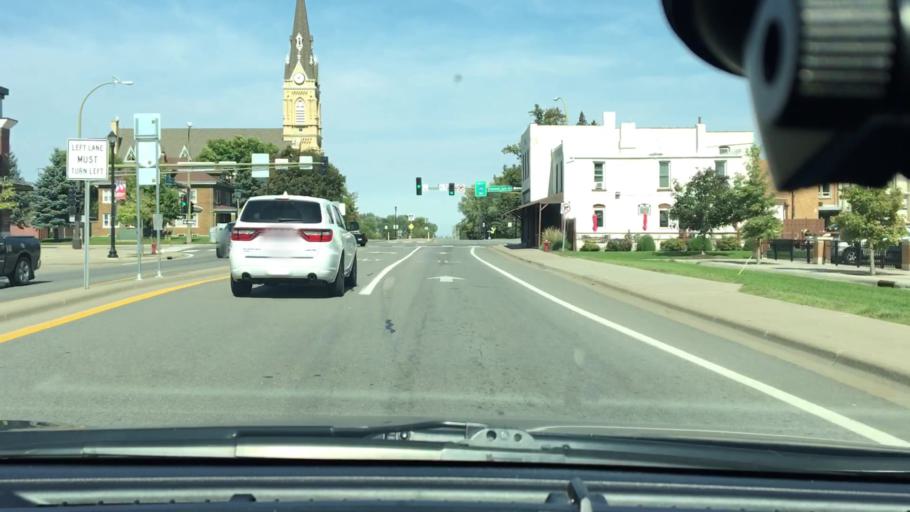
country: US
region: Minnesota
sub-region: Wright County
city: Saint Michael
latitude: 45.2095
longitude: -93.6647
